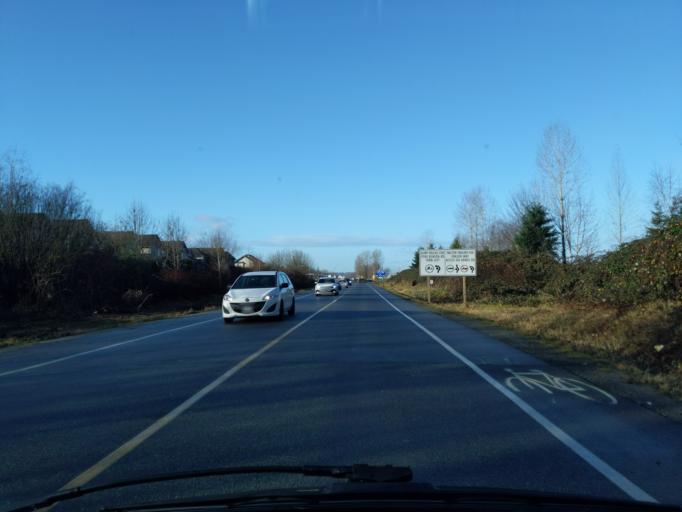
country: CA
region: British Columbia
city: Pitt Meadows
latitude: 49.2084
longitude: -122.6749
